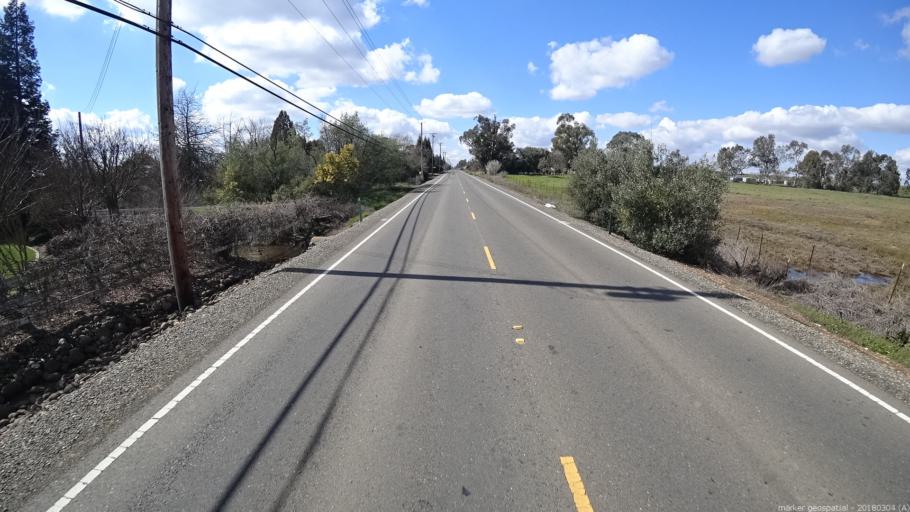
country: US
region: California
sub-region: Sacramento County
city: Vineyard
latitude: 38.4817
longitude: -121.3010
